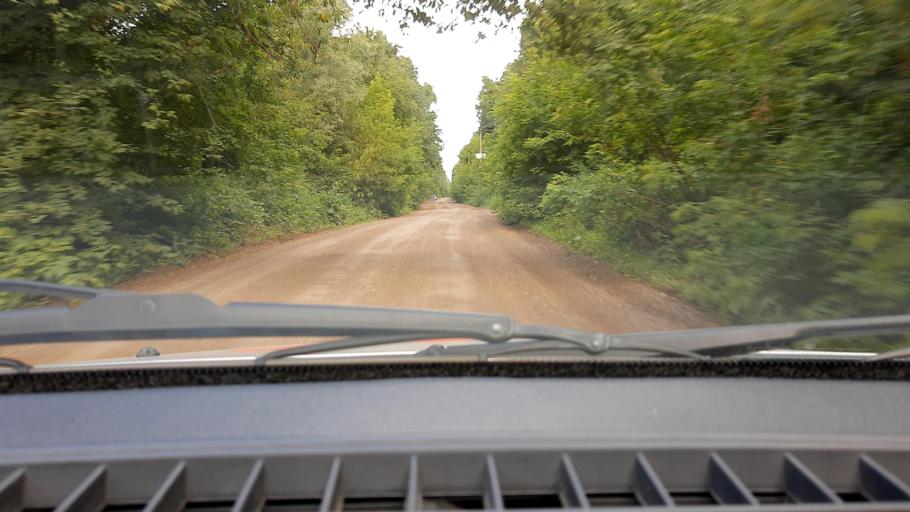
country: RU
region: Bashkortostan
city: Ufa
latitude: 54.6866
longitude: 56.0544
